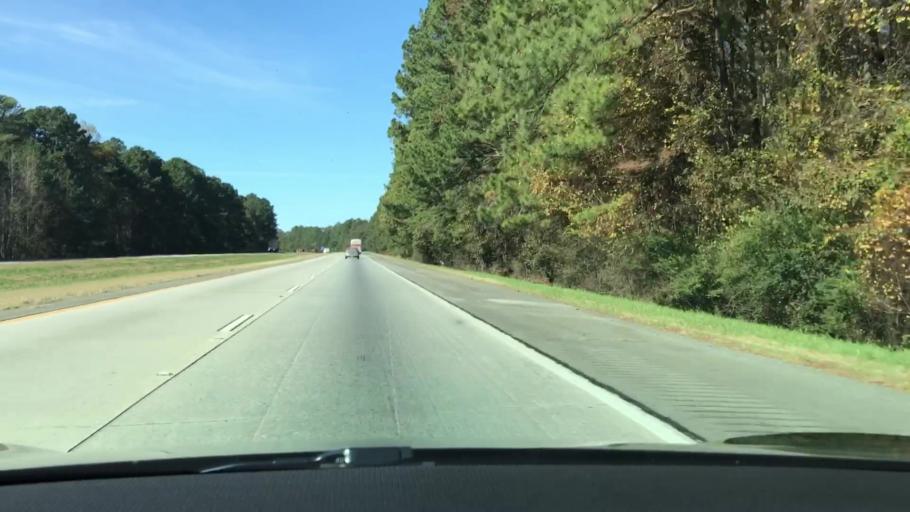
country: US
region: Georgia
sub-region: Greene County
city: Union Point
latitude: 33.5493
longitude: -83.0486
